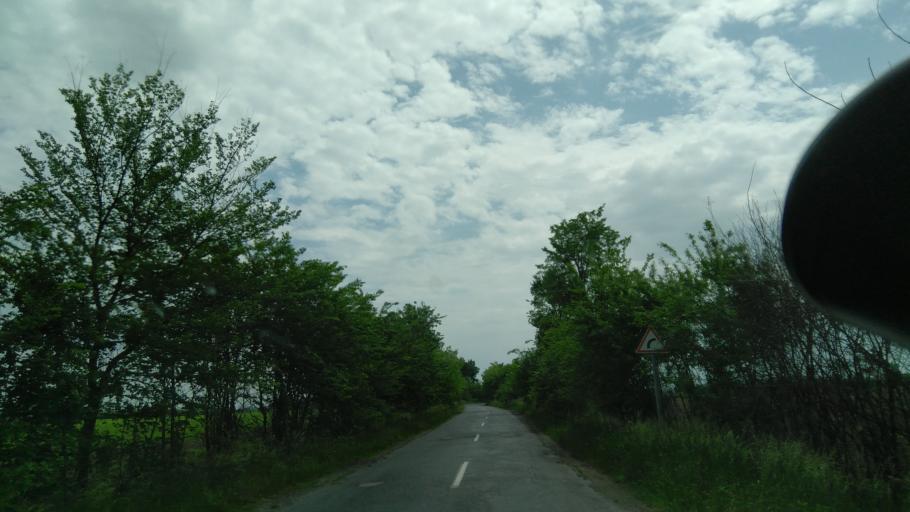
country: RO
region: Bihor
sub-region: Comuna Sannicolau-Roman
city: Sannicolau Roman
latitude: 47.0020
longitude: 21.6188
